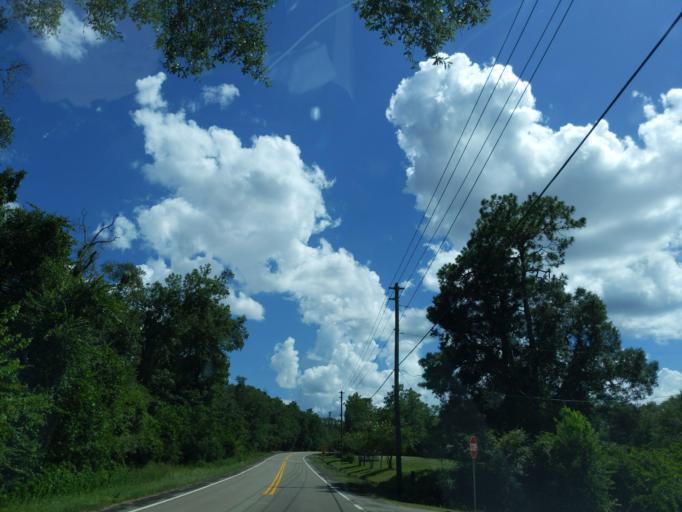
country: US
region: Florida
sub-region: Leon County
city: Tallahassee
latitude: 30.4033
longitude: -84.3332
